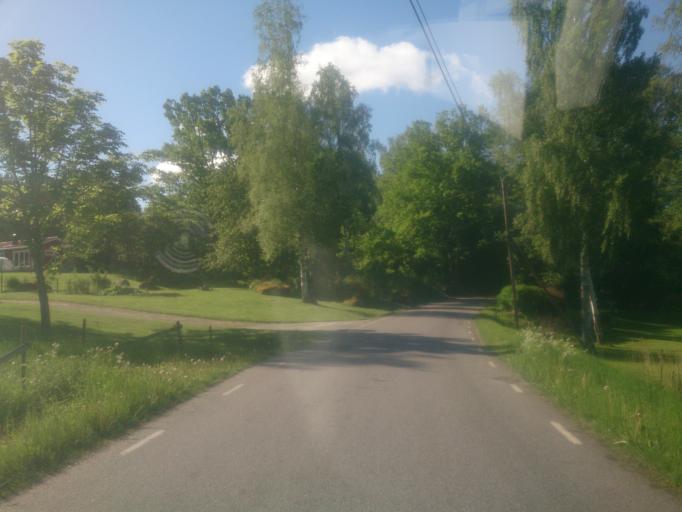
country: SE
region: OEstergoetland
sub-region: Atvidabergs Kommun
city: Atvidaberg
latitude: 58.3093
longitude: 16.0770
